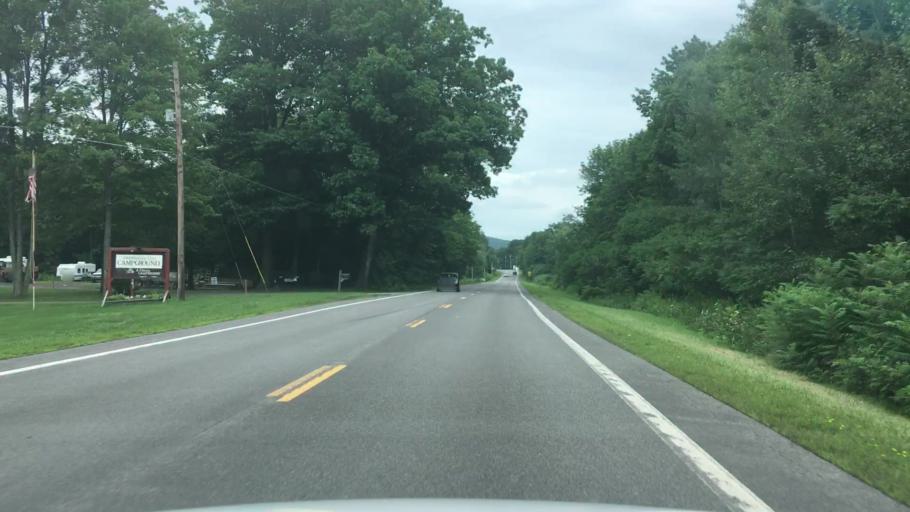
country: US
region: New York
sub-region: Otsego County
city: West End
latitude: 42.4373
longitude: -75.1175
